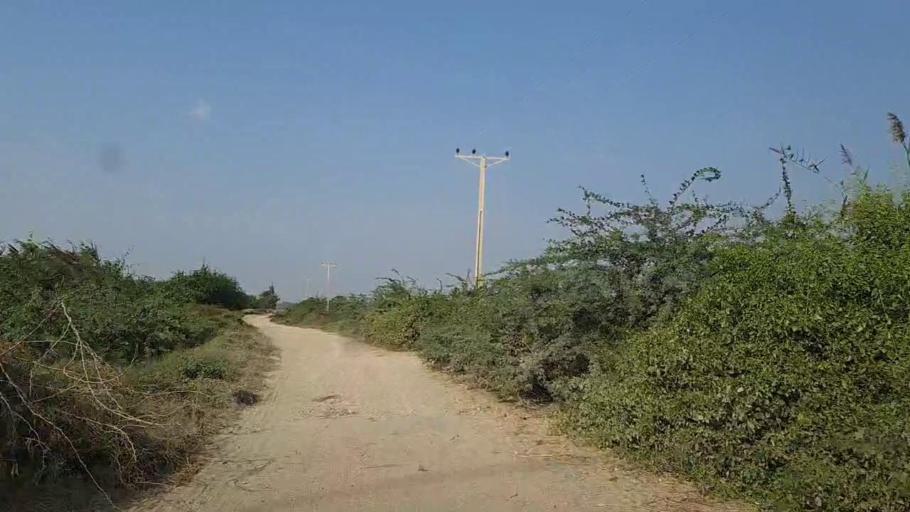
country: PK
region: Sindh
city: Mirpur Sakro
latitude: 24.5806
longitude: 67.5678
